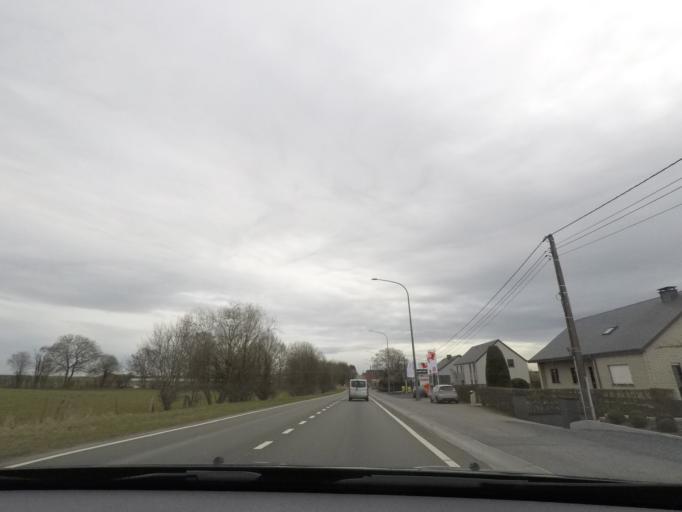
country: BE
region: Wallonia
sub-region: Province du Luxembourg
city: Bastogne
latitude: 49.9934
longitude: 5.7330
